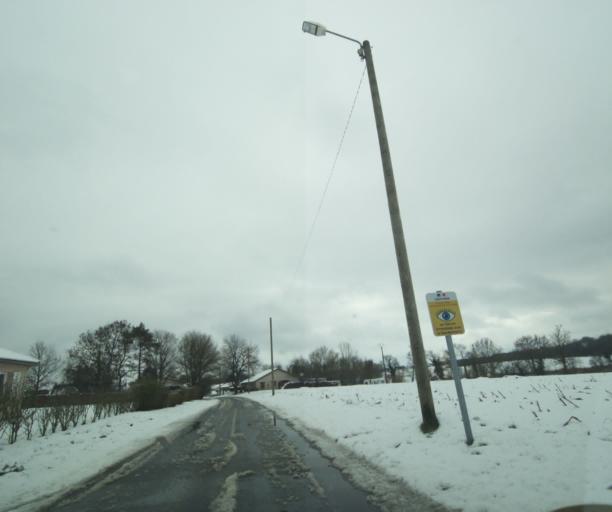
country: FR
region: Champagne-Ardenne
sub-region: Departement de la Haute-Marne
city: Montier-en-Der
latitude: 48.4142
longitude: 4.7353
